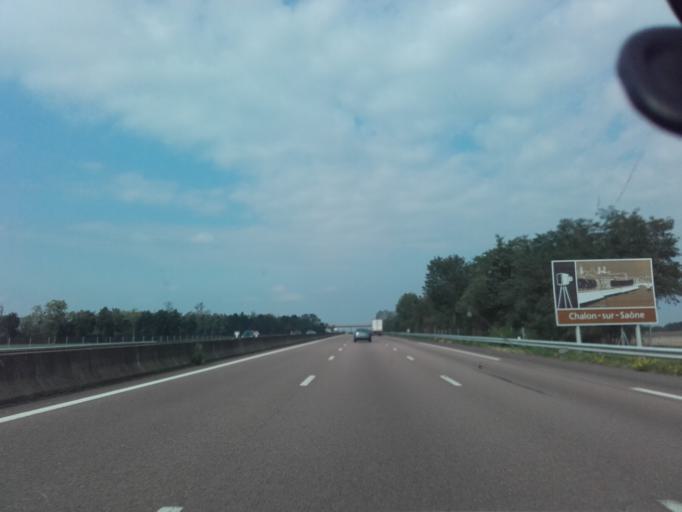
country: FR
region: Bourgogne
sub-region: Departement de Saone-et-Loire
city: Sevrey
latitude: 46.7154
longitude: 4.8399
